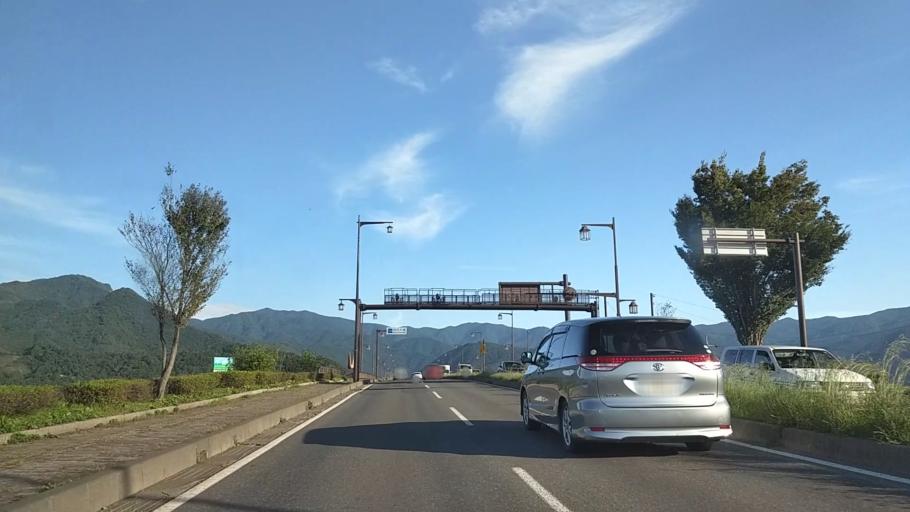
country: JP
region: Nagano
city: Nagano-shi
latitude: 36.5837
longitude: 138.1904
